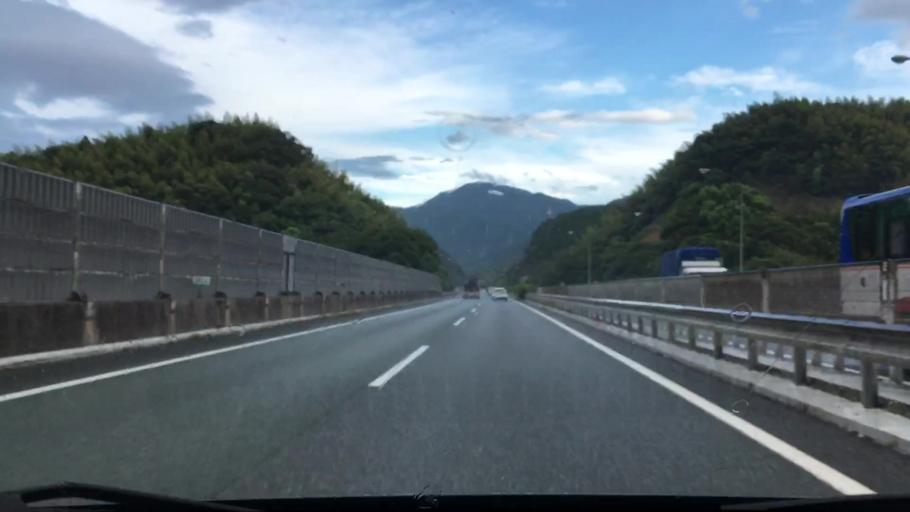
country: JP
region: Fukuoka
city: Kitakyushu
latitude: 33.8042
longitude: 130.8519
